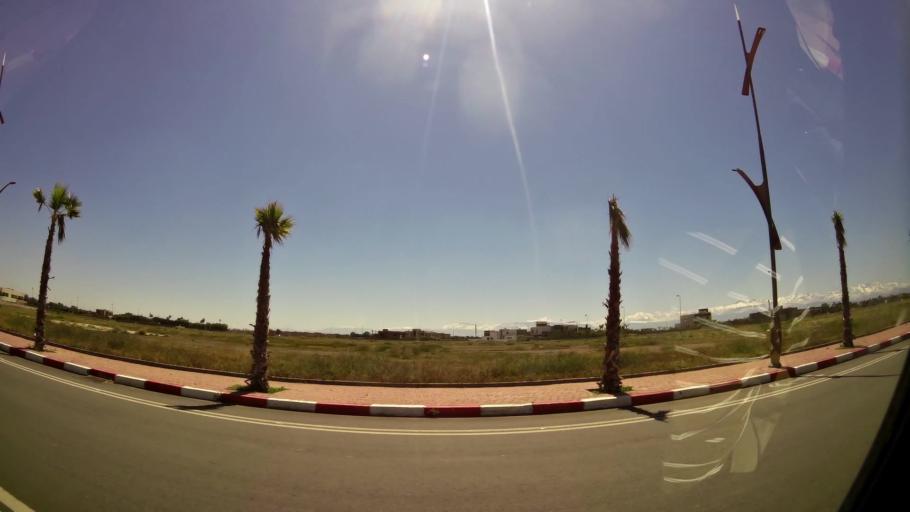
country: MA
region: Marrakech-Tensift-Al Haouz
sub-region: Marrakech
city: Marrakesh
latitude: 31.5964
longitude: -8.0039
